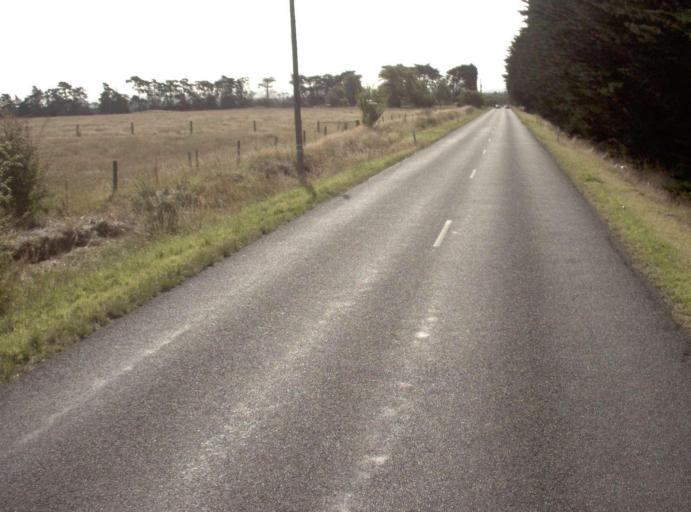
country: AU
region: Victoria
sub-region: Latrobe
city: Morwell
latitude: -38.2922
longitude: 146.4386
